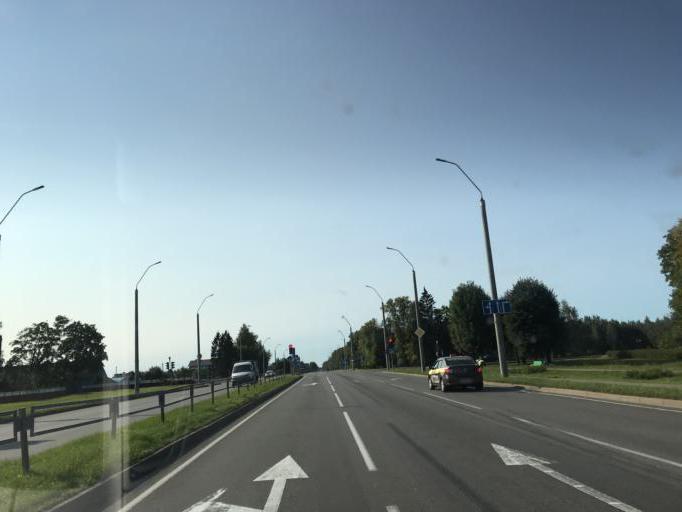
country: BY
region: Mogilev
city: Buynichy
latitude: 53.8604
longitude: 30.2576
